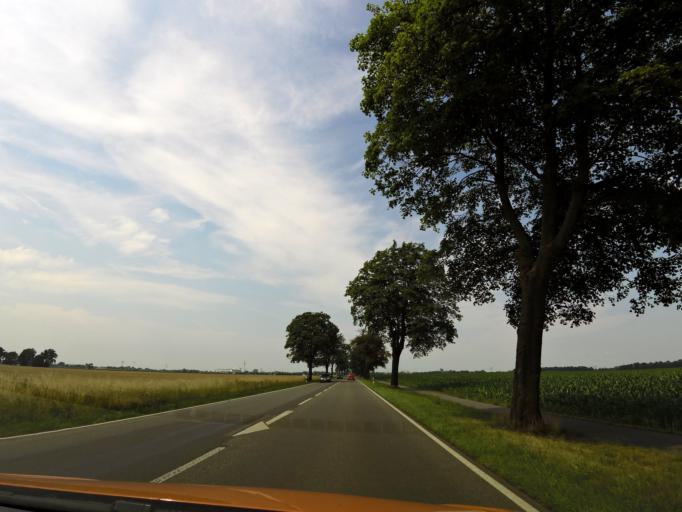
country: DE
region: Brandenburg
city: Kyritz
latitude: 52.9269
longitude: 12.4201
